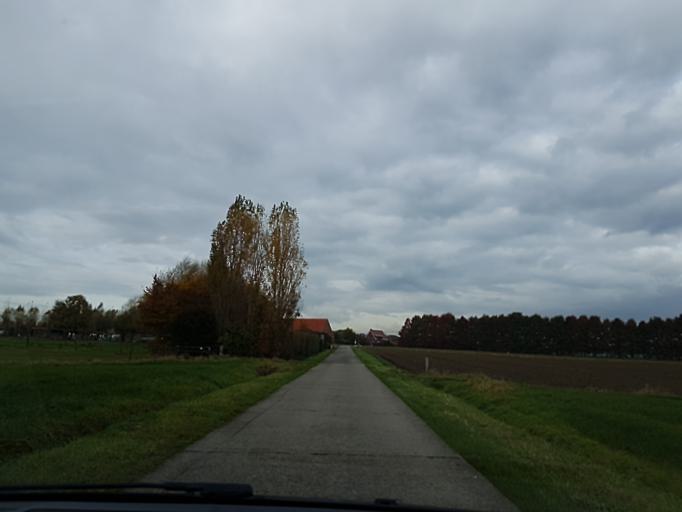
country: BE
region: Flanders
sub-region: Provincie Antwerpen
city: Boechout
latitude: 51.1646
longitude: 4.5322
